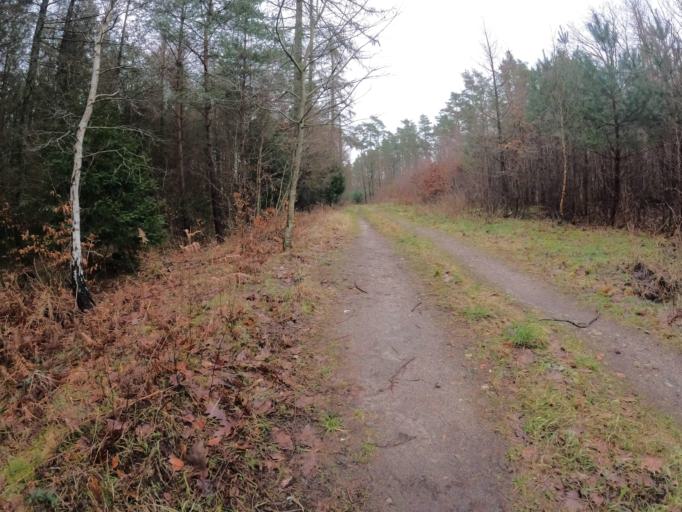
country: PL
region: West Pomeranian Voivodeship
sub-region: Powiat slawienski
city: Darlowo
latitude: 54.3965
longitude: 16.4565
